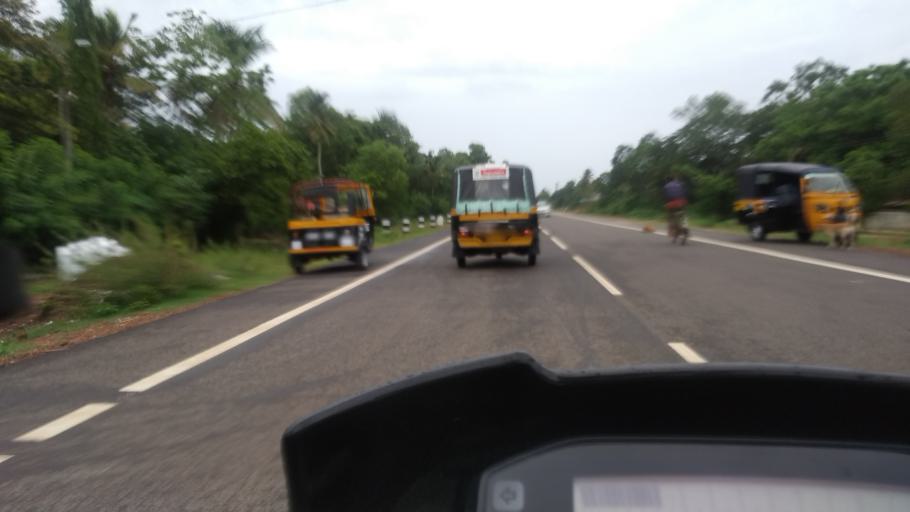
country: IN
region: Kerala
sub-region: Alappuzha
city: Alleppey
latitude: 9.5092
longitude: 76.3246
